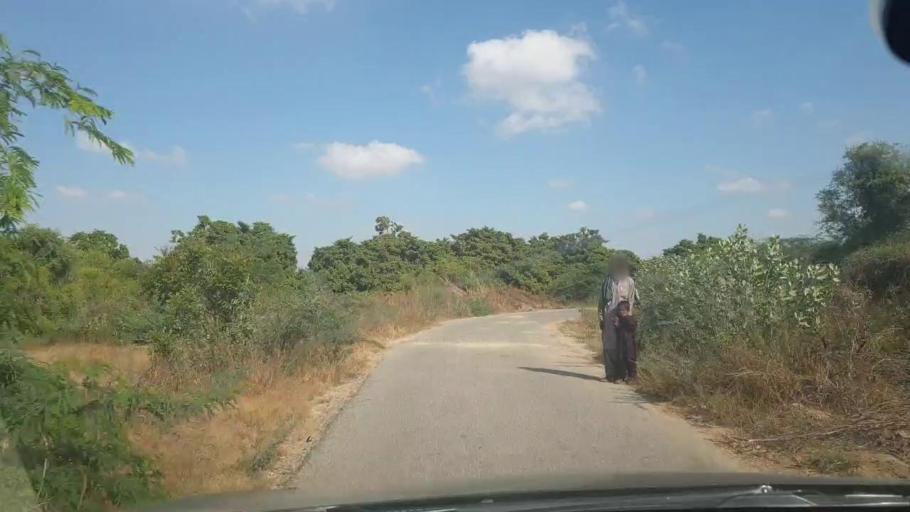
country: PK
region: Sindh
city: Malir Cantonment
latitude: 25.0561
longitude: 67.3902
